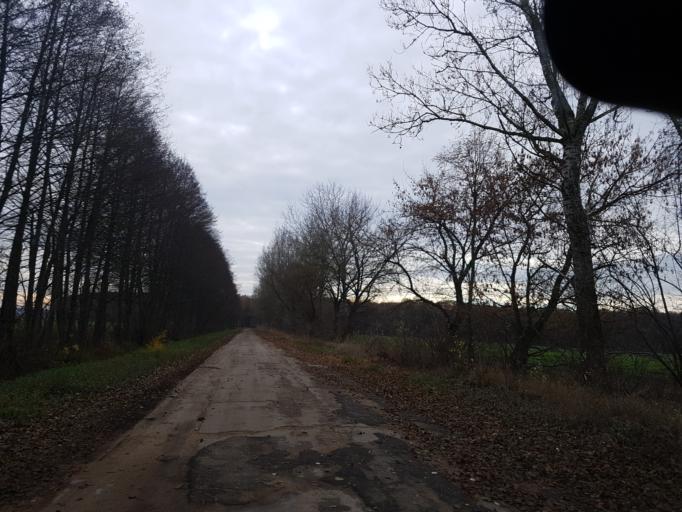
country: DE
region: Brandenburg
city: Treuenbrietzen
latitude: 52.0952
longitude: 12.9328
